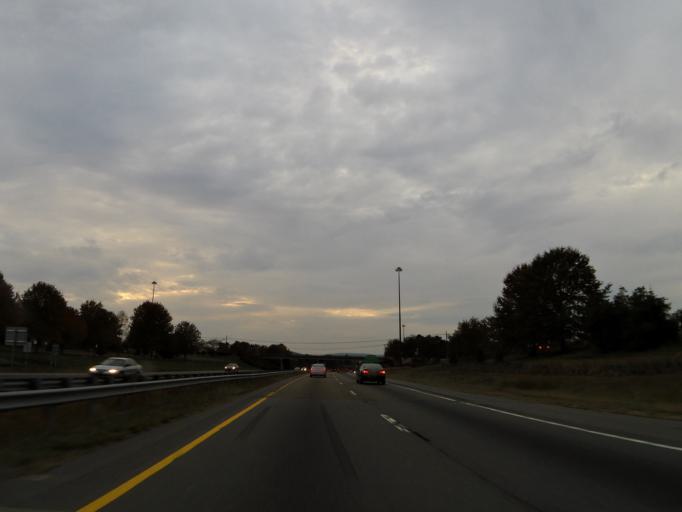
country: US
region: North Carolina
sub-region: Burke County
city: Hildebran
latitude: 35.7056
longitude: -81.4212
